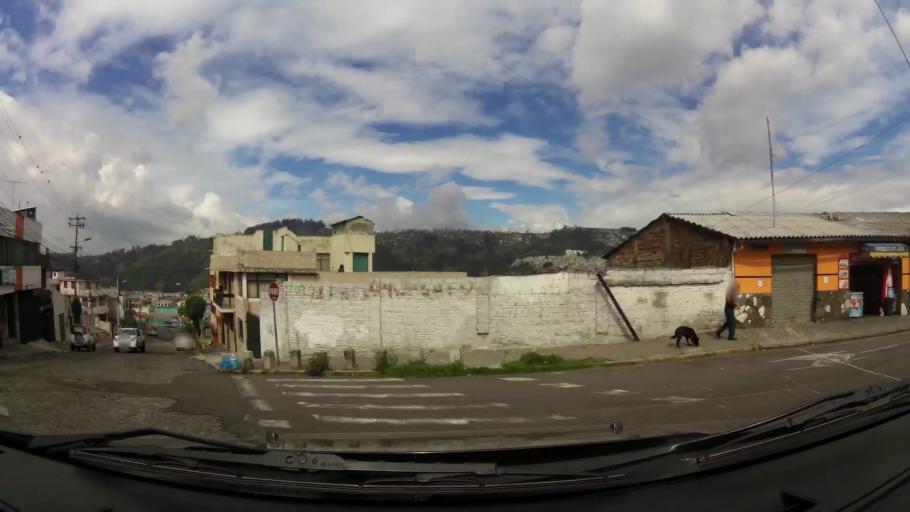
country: EC
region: Pichincha
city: Quito
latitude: -0.2180
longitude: -78.4928
